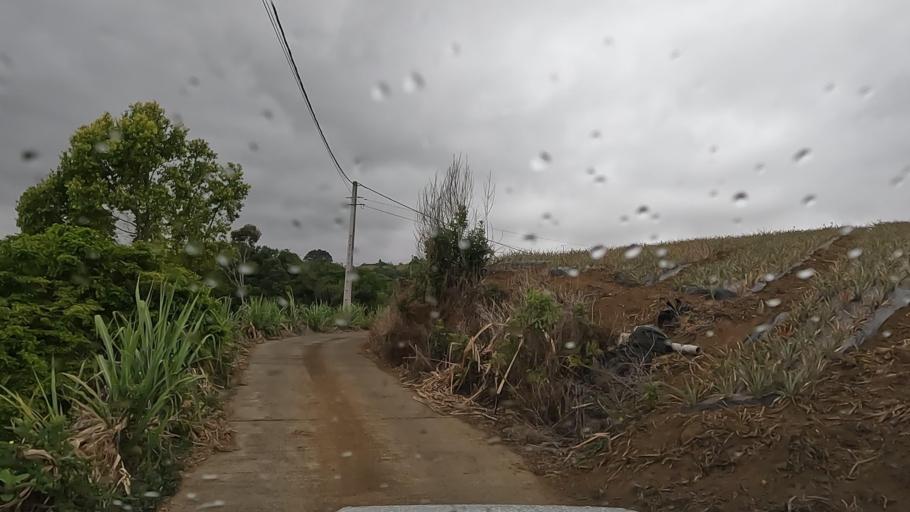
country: RE
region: Reunion
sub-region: Reunion
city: Le Tampon
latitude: -21.2906
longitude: 55.5436
